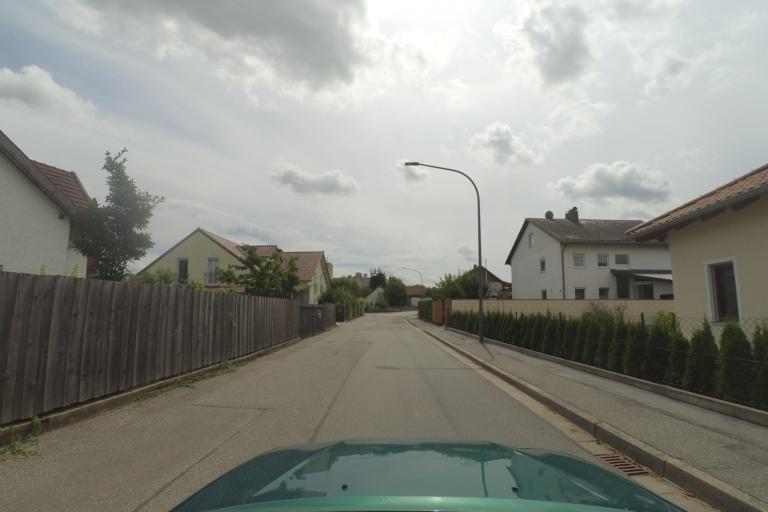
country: DE
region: Bavaria
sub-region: Lower Bavaria
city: Geiselhoring
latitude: 48.8240
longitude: 12.3872
